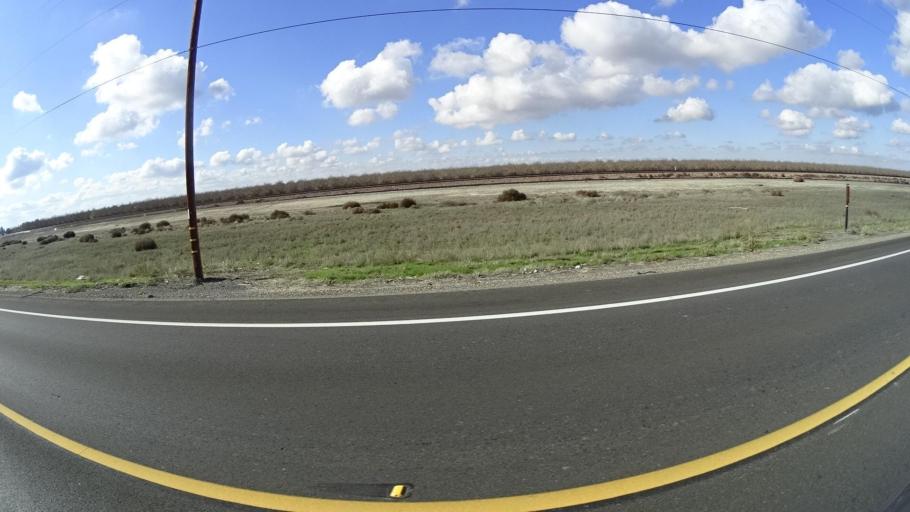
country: US
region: California
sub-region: Kern County
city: Wasco
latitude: 35.6771
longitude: -119.3301
